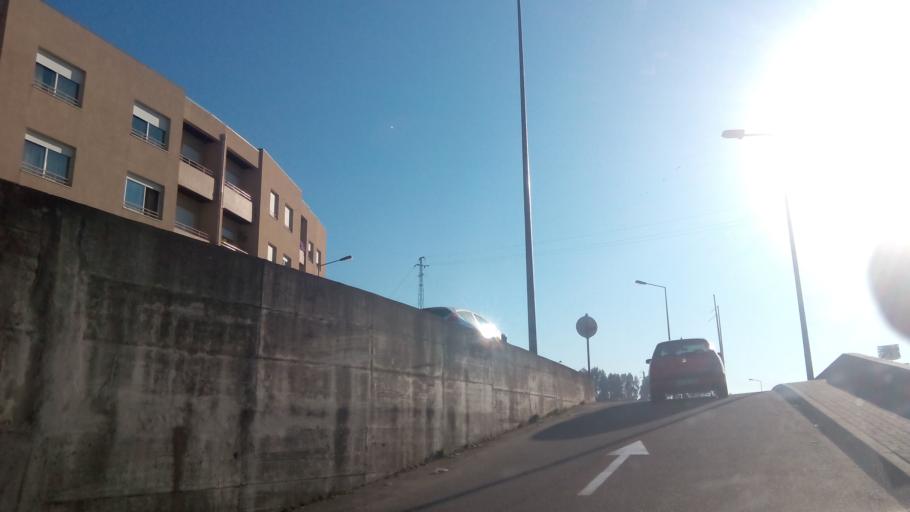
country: PT
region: Porto
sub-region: Paredes
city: Casteloes de Cepeda
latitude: 41.2006
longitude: -8.3463
